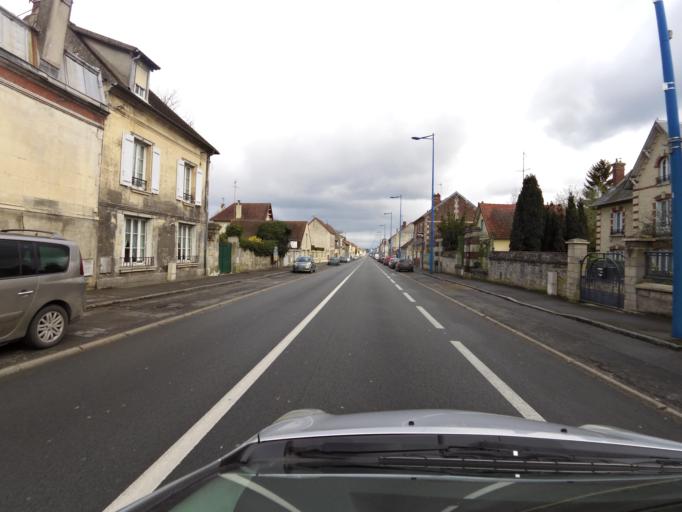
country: FR
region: Picardie
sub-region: Departement de l'Oise
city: Pont-Sainte-Maxence
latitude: 49.2937
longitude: 2.6048
